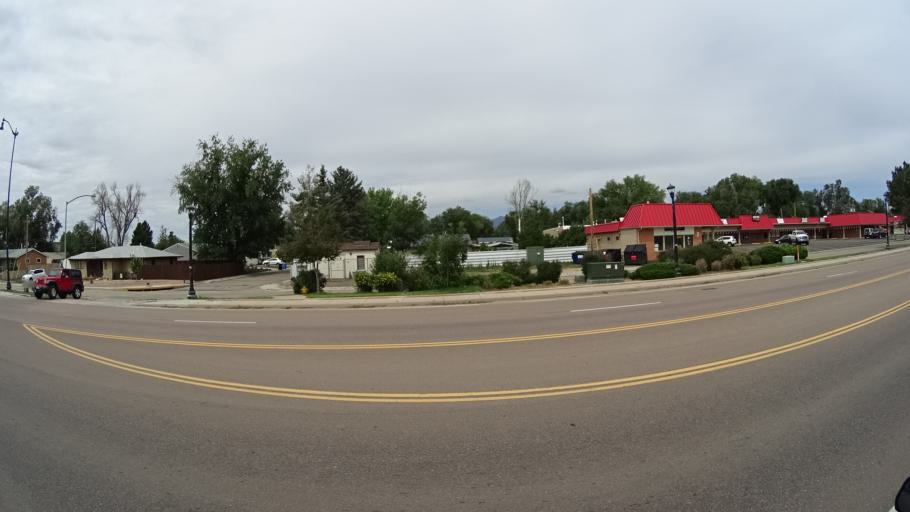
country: US
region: Colorado
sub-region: El Paso County
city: Fountain
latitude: 38.6884
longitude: -104.7045
